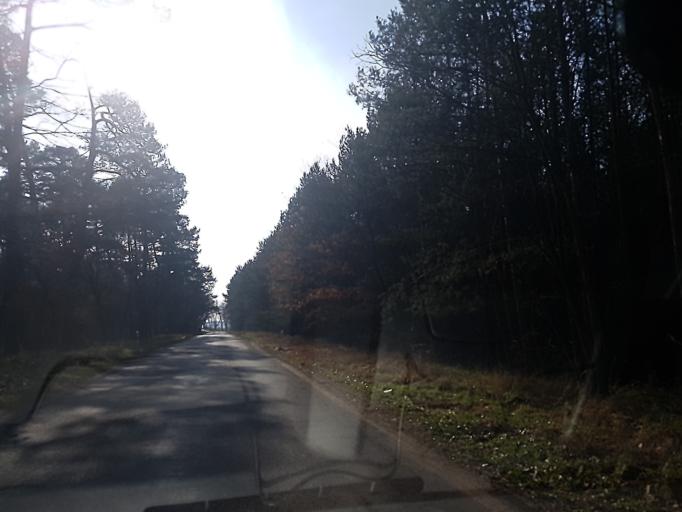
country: DE
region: Brandenburg
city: Wenzlow
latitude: 52.3228
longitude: 12.4419
